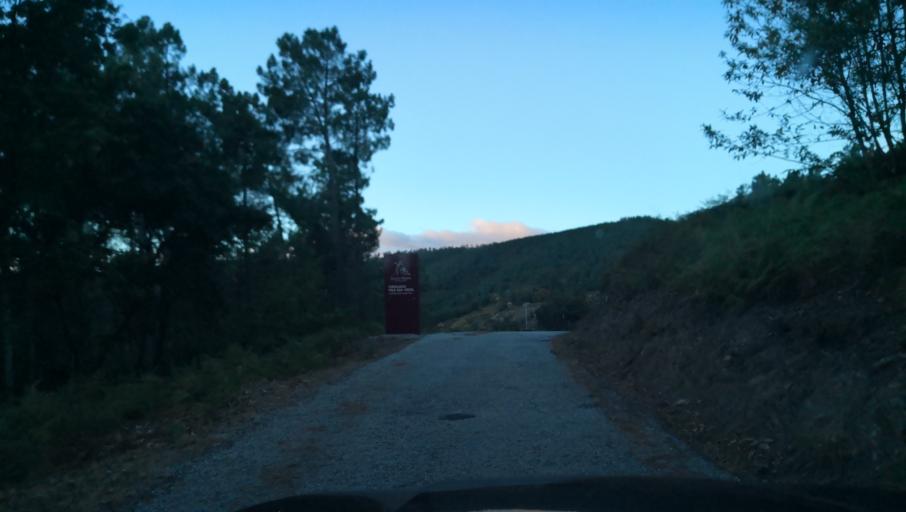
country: PT
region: Vila Real
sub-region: Santa Marta de Penaguiao
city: Santa Marta de Penaguiao
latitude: 41.2629
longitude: -7.8288
